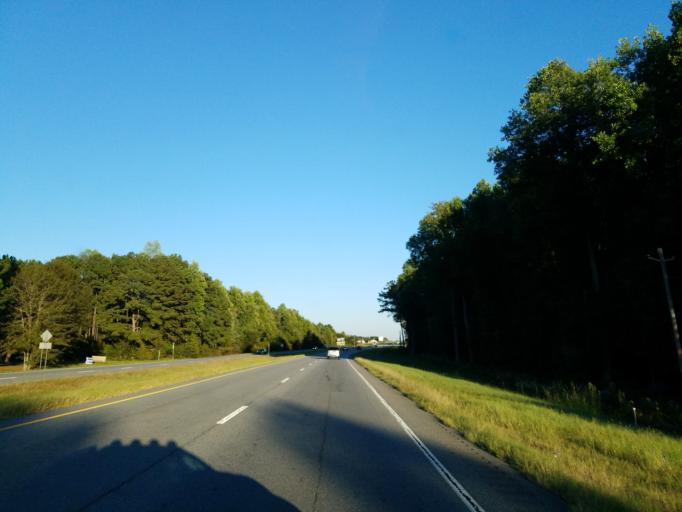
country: US
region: Georgia
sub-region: Worth County
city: Sylvester
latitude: 31.5081
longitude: -83.7378
